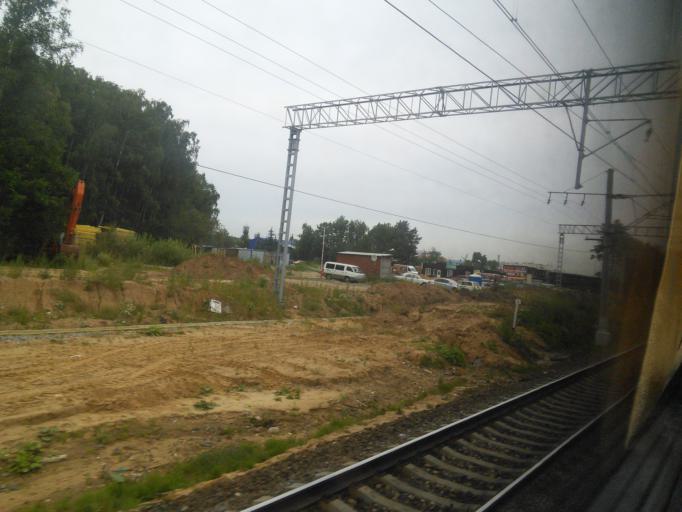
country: RU
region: Moskovskaya
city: Novoivanovskoye
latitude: 55.7058
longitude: 37.3508
